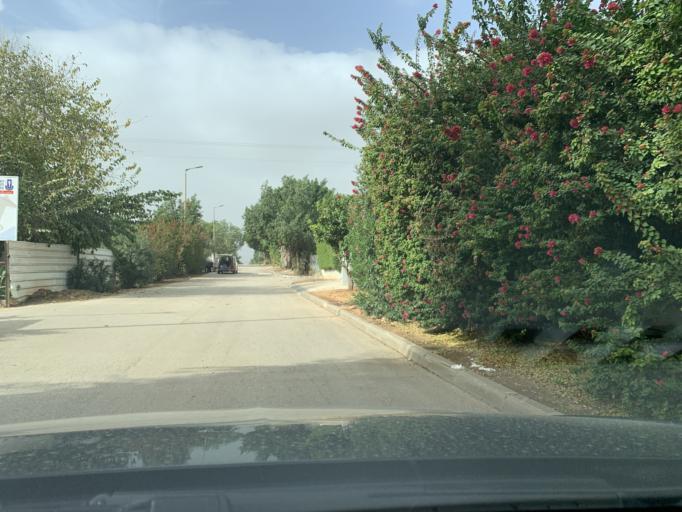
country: IL
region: Central District
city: Jaljulya
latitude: 32.1577
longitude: 34.9449
